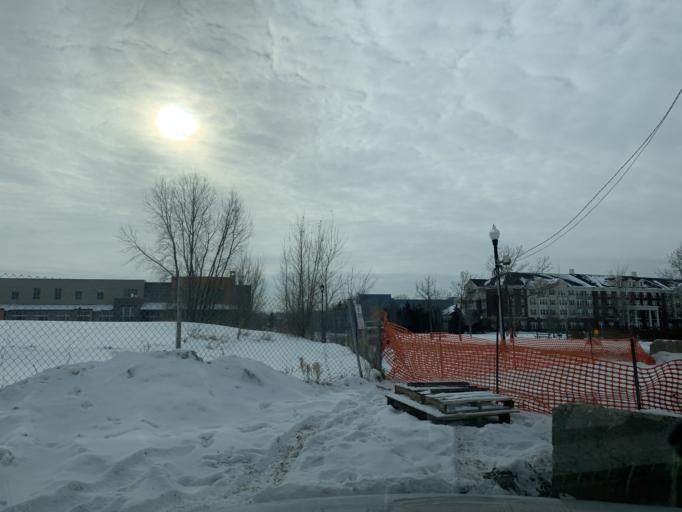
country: US
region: Minnesota
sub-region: Hennepin County
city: Minneapolis
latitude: 44.9827
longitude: -93.2929
